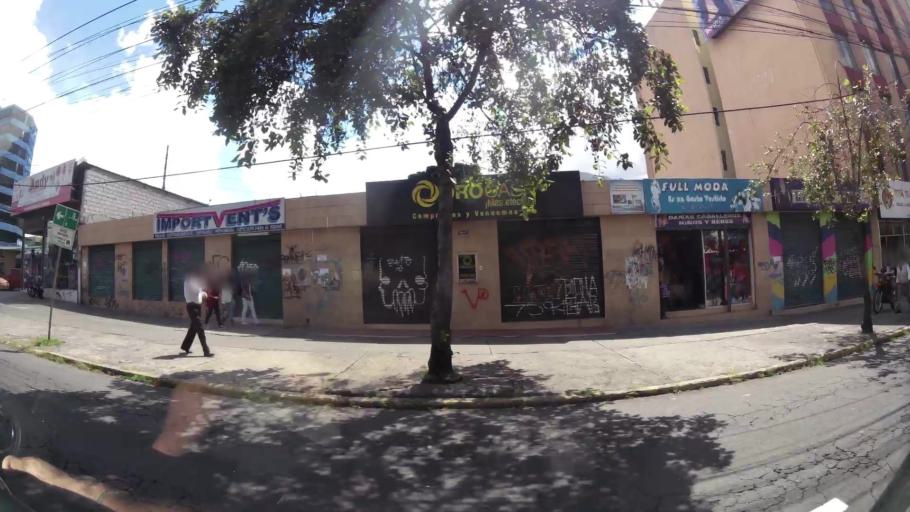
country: EC
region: Pichincha
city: Quito
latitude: -0.2055
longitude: -78.4993
